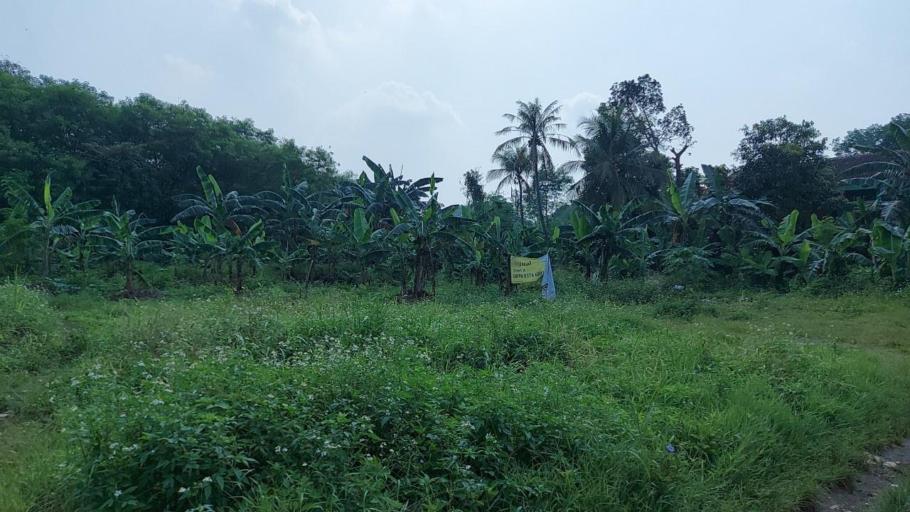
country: ID
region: West Java
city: Cibinong
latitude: -6.5275
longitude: 106.8342
